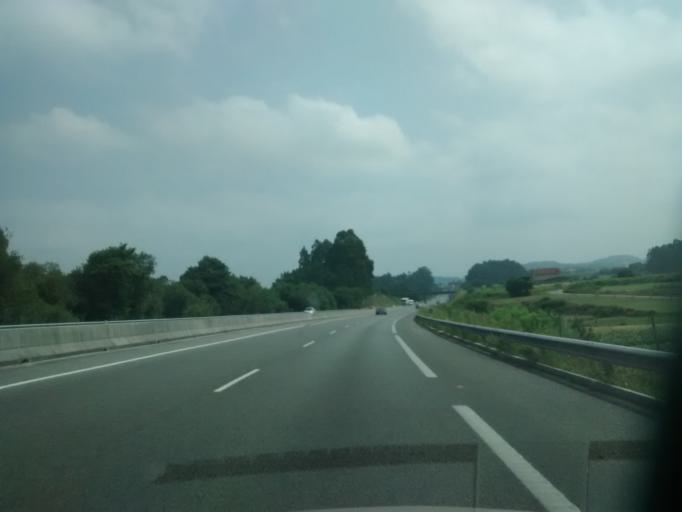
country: ES
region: Galicia
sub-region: Provincia de Pontevedra
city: Meis
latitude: 42.5061
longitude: -8.7166
